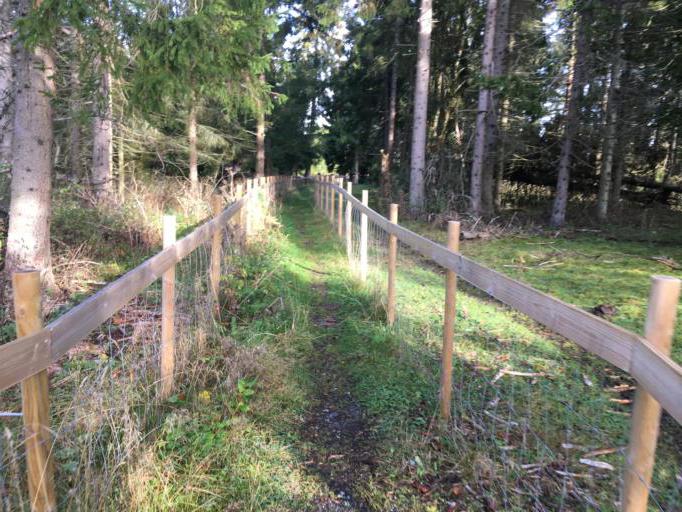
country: NO
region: Nord-Trondelag
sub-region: Leksvik
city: Leksvik
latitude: 63.5730
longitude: 10.6130
